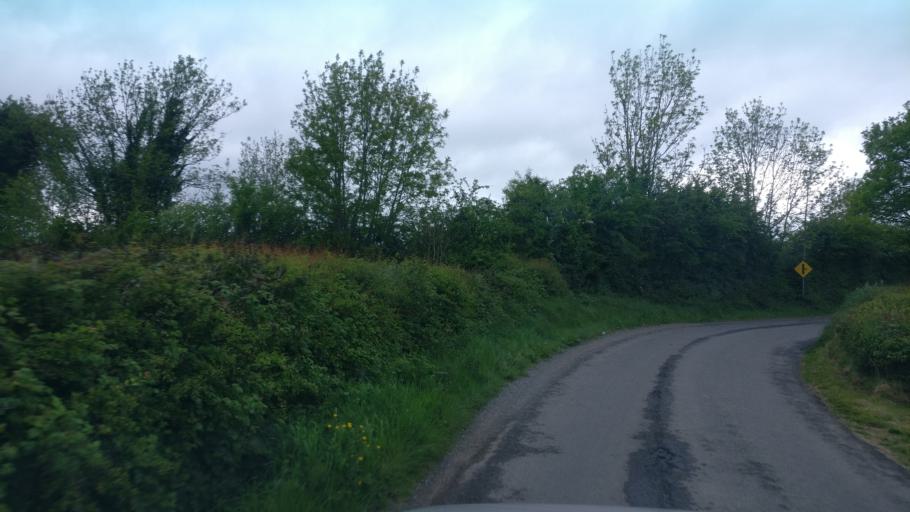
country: IE
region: Connaught
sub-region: County Galway
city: Portumna
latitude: 53.1337
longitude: -8.2922
